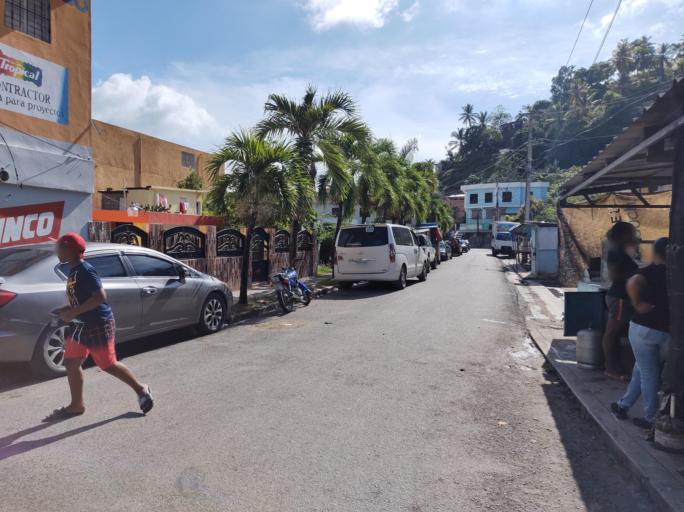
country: DO
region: Samana
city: Samana
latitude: 19.2040
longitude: -69.3432
